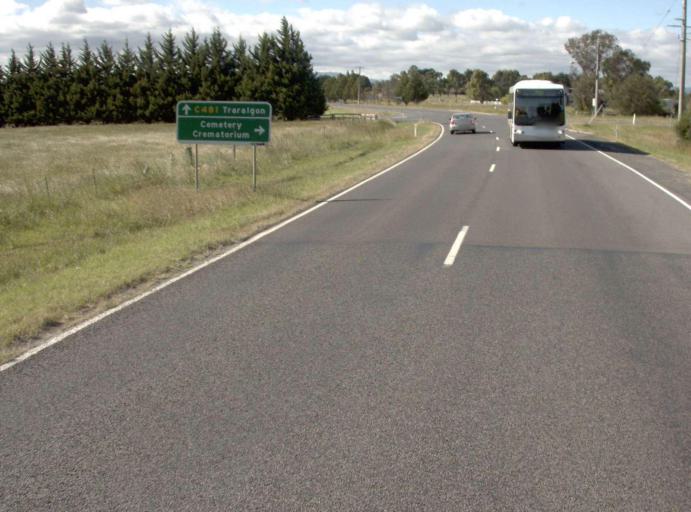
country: AU
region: Victoria
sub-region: Latrobe
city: Traralgon
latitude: -38.1809
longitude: 146.5002
